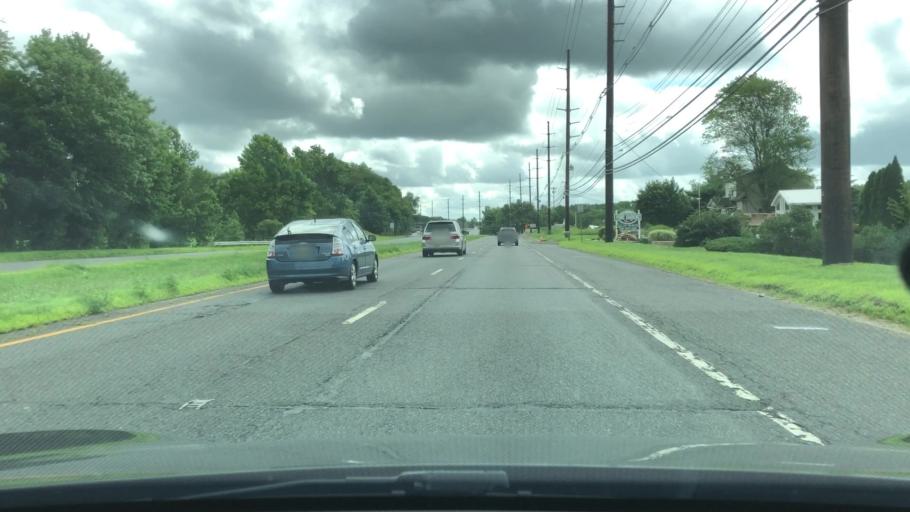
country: US
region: New Jersey
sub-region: Mercer County
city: Twin Rivers
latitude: 40.2623
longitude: -74.4429
